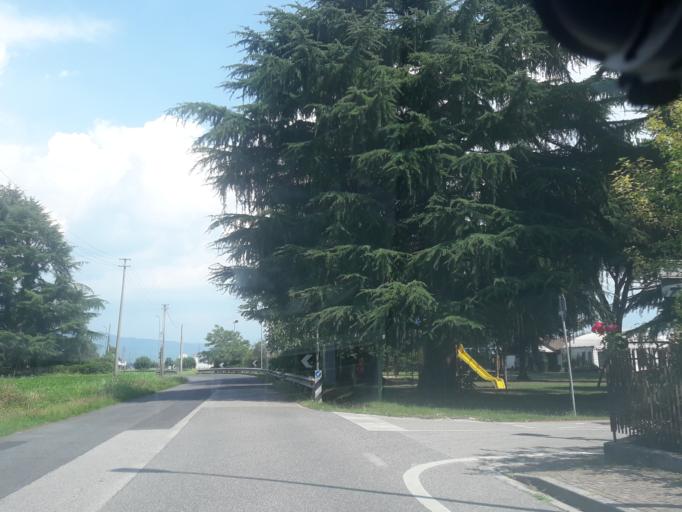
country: IT
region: Friuli Venezia Giulia
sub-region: Provincia di Udine
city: Reana del Roiale
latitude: 46.1284
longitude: 13.2178
